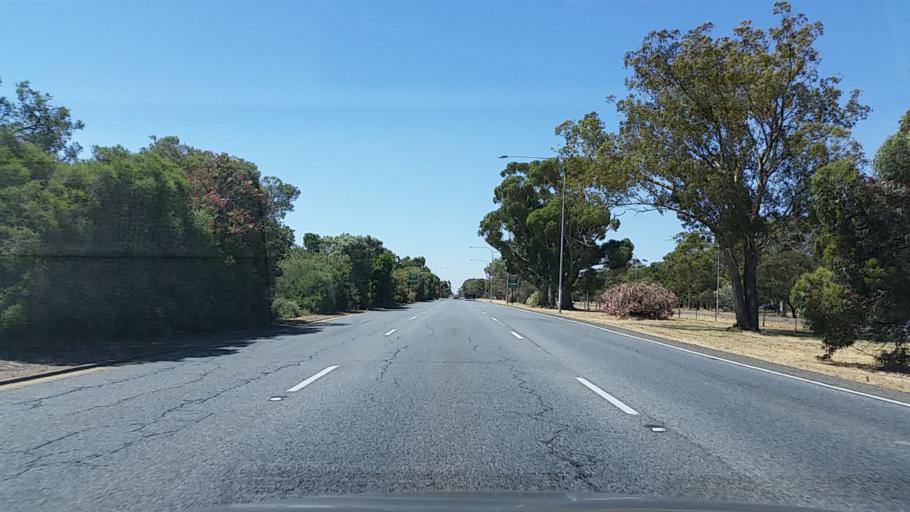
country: AU
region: South Australia
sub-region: Salisbury
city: Elizabeth
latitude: -34.7021
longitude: 138.6816
